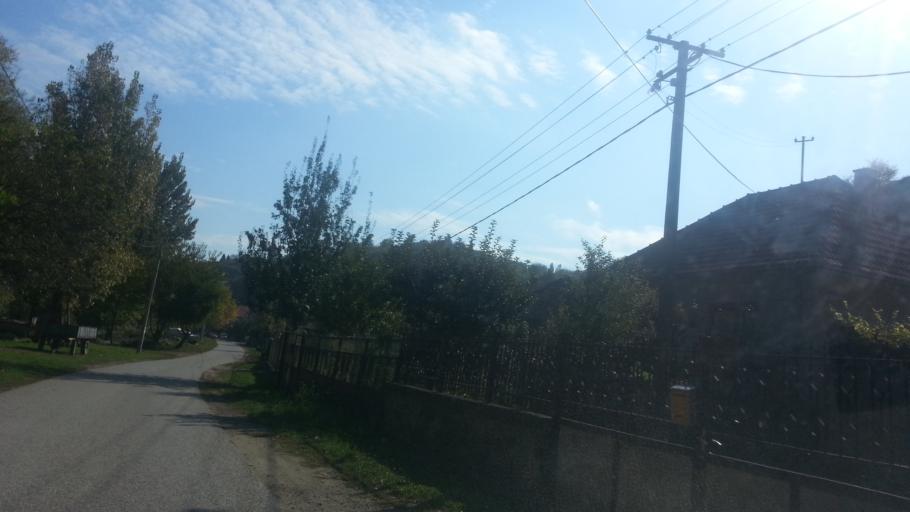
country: RS
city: Novi Slankamen
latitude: 45.1499
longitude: 20.2484
